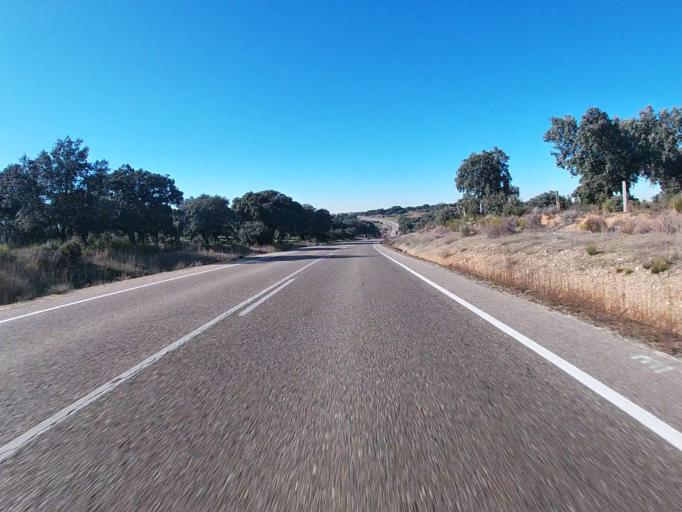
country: ES
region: Castille and Leon
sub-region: Provincia de Salamanca
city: Juzbado
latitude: 41.0768
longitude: -5.8415
